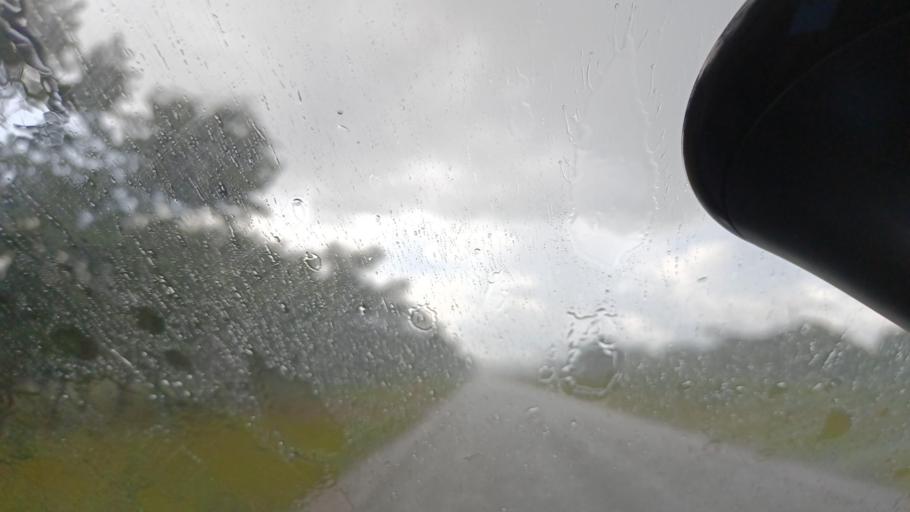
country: ZM
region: North-Western
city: Kasempa
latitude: -13.0971
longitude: 25.9076
